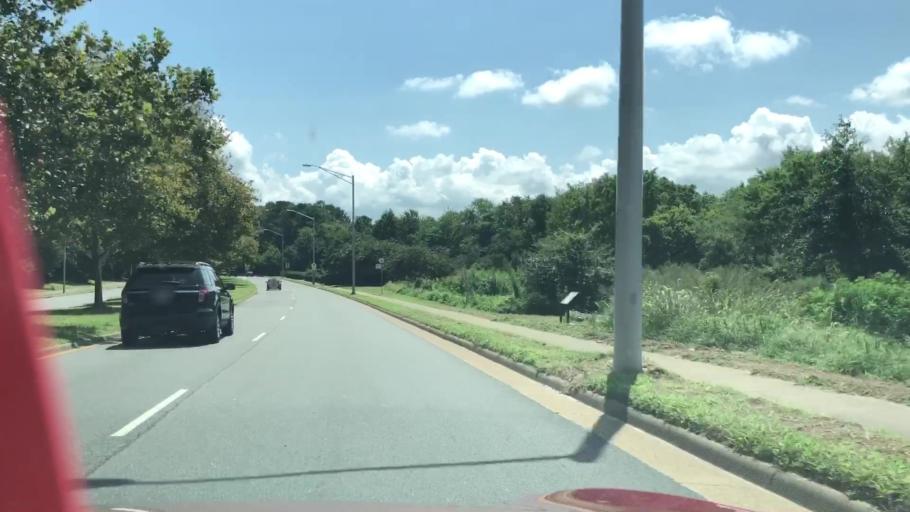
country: US
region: Virginia
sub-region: City of Virginia Beach
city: Virginia Beach
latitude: 36.9001
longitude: -76.0659
